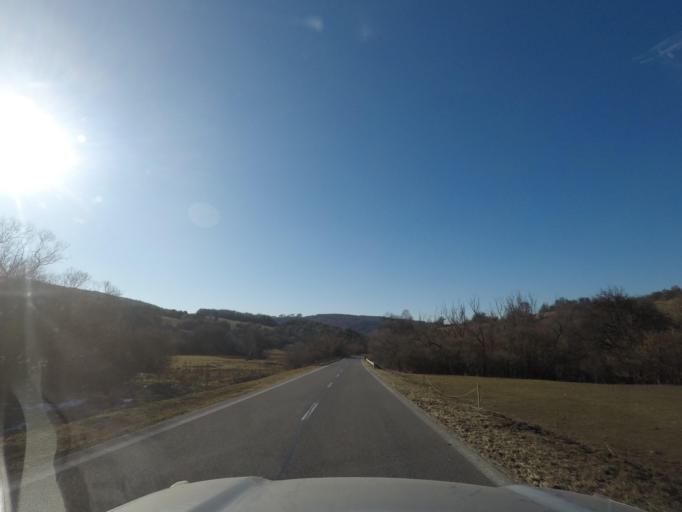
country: PL
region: Subcarpathian Voivodeship
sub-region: Powiat sanocki
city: Komancza
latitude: 49.1605
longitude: 22.0477
